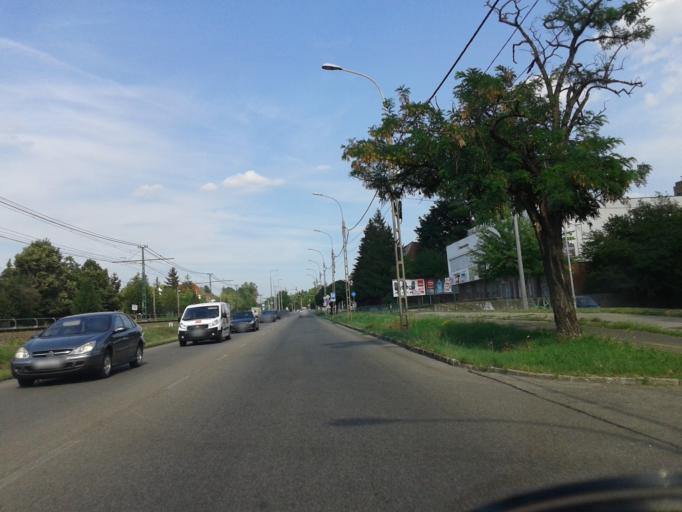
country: HU
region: Budapest
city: Budapest XVI. keruelet
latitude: 47.5104
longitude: 19.1878
